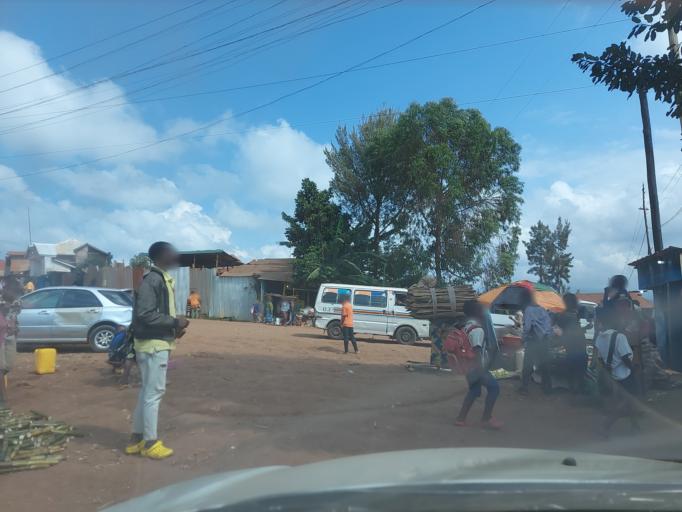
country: CD
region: South Kivu
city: Bukavu
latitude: -2.5134
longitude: 28.8380
